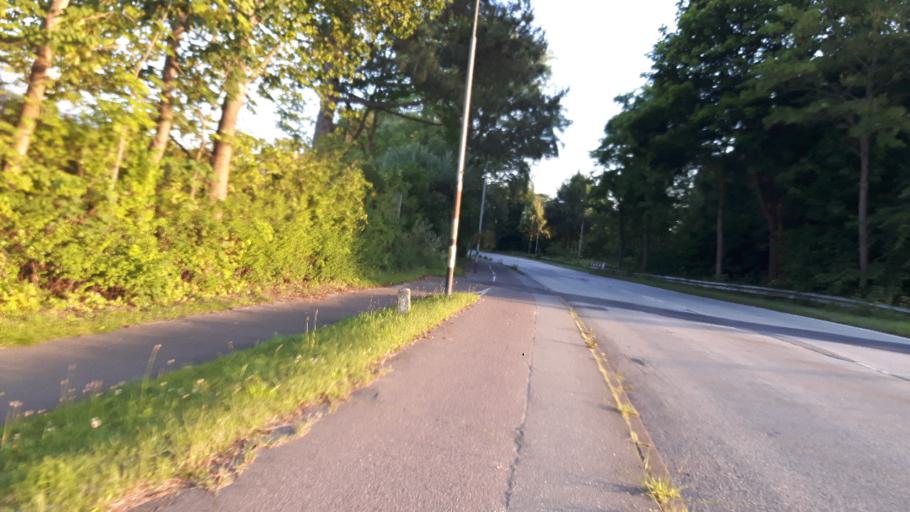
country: DE
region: Schleswig-Holstein
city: Travemuende
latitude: 53.9539
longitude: 10.8551
